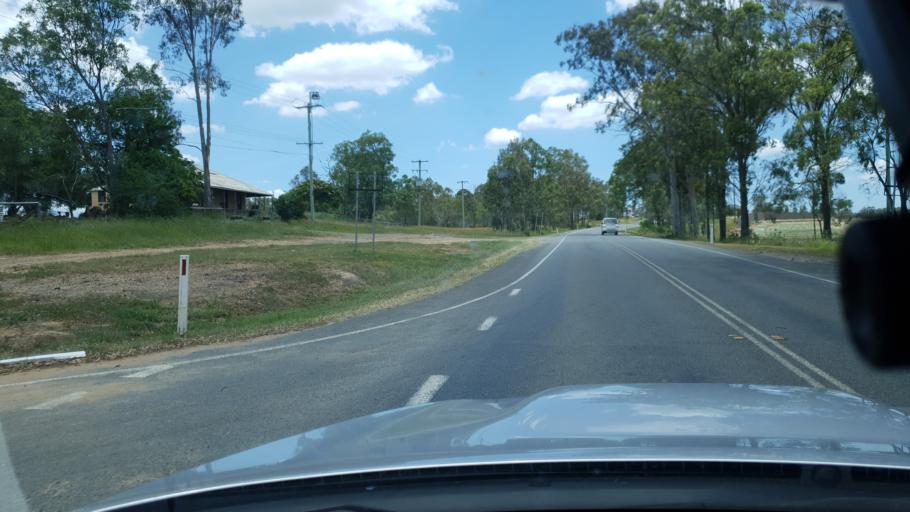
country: AU
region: Queensland
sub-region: Logan
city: North Maclean
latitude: -27.7424
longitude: 152.9850
